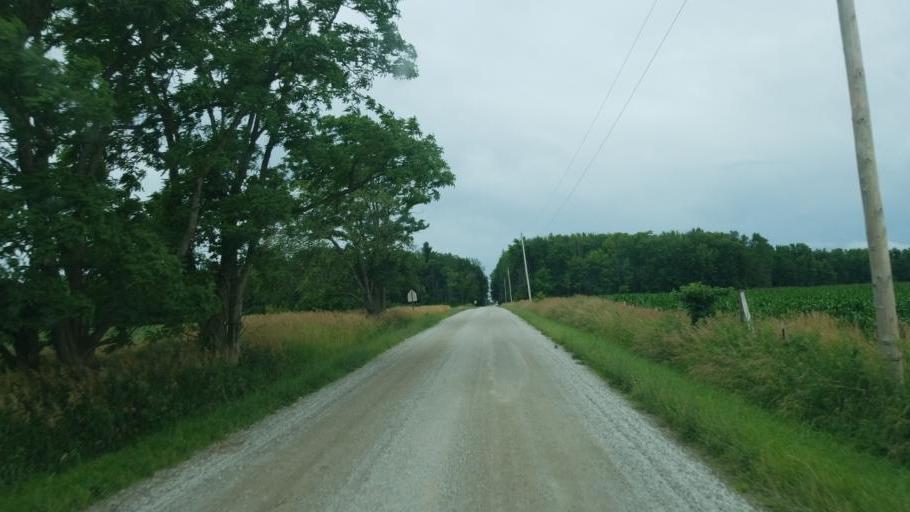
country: US
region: Ohio
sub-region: Huron County
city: Greenwich
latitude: 40.9503
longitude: -82.4314
